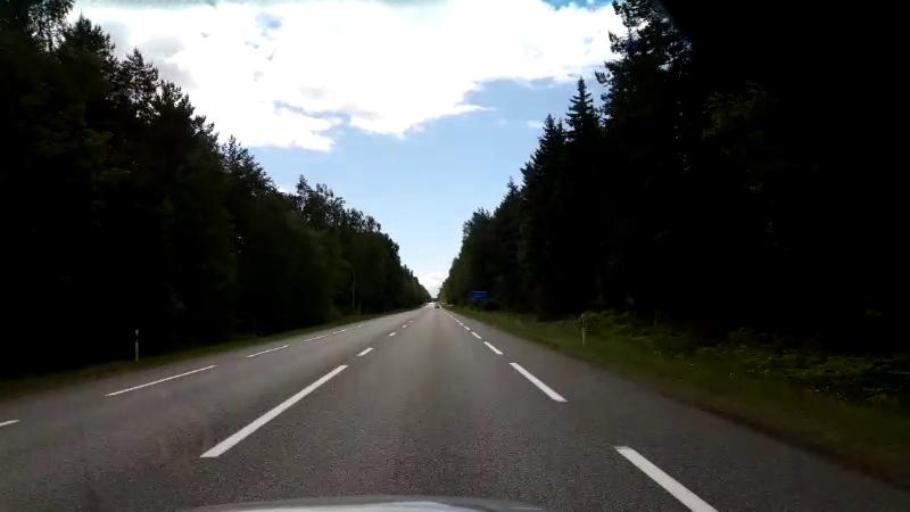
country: LV
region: Saulkrastu
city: Saulkrasti
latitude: 57.4871
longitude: 24.4323
